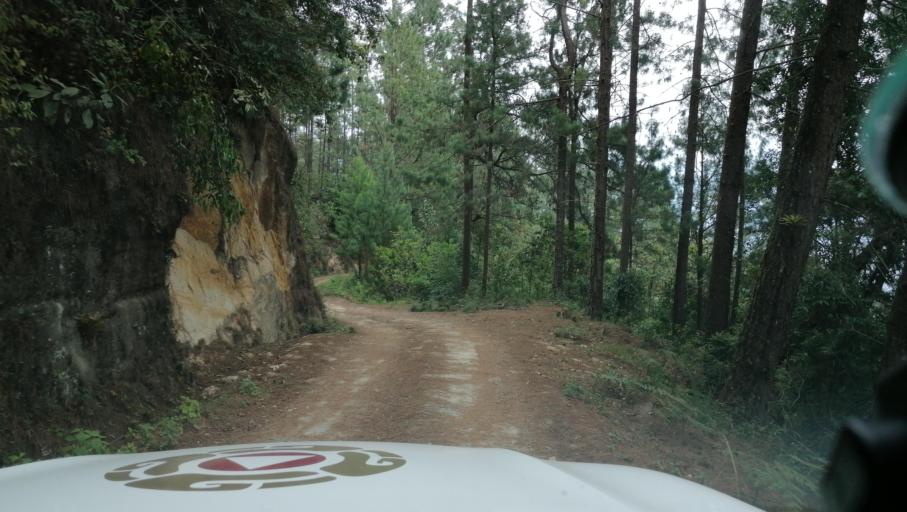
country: MX
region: Chiapas
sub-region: Tapachula
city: Canton Villaflor
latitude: 15.2020
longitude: -92.2325
